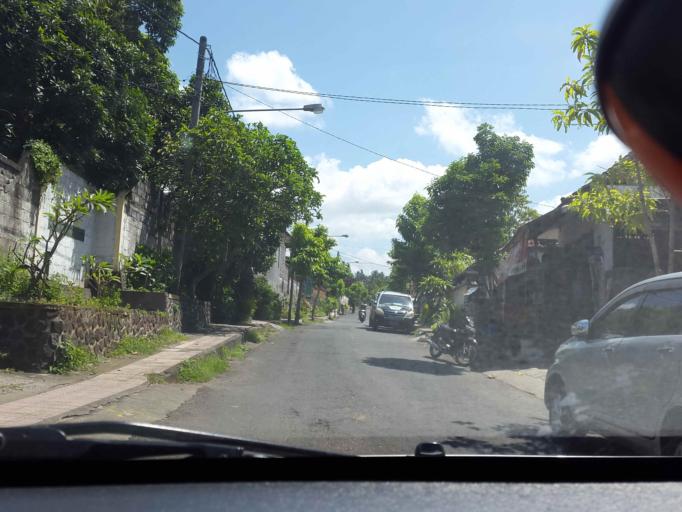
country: ID
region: Bali
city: Klungkung
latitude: -8.5376
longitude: 115.3947
